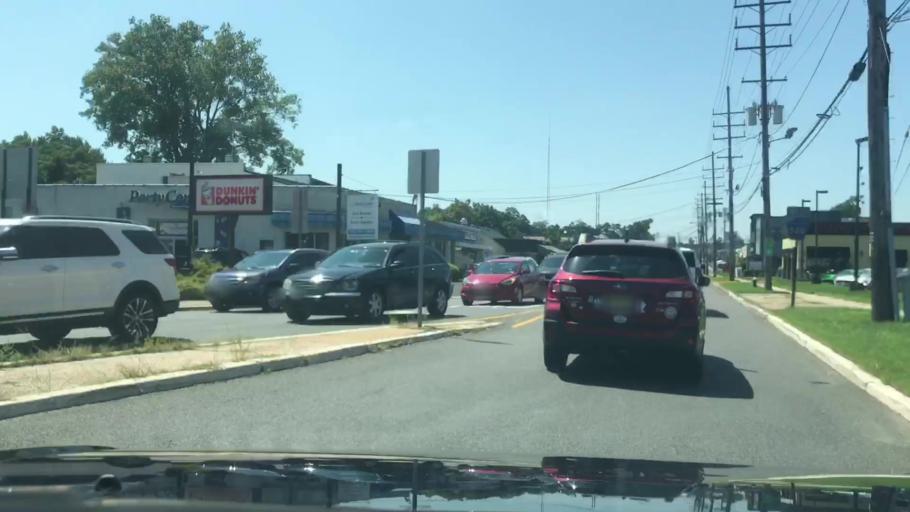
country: US
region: New Jersey
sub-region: Monmouth County
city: Red Bank
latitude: 40.3383
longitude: -74.0639
